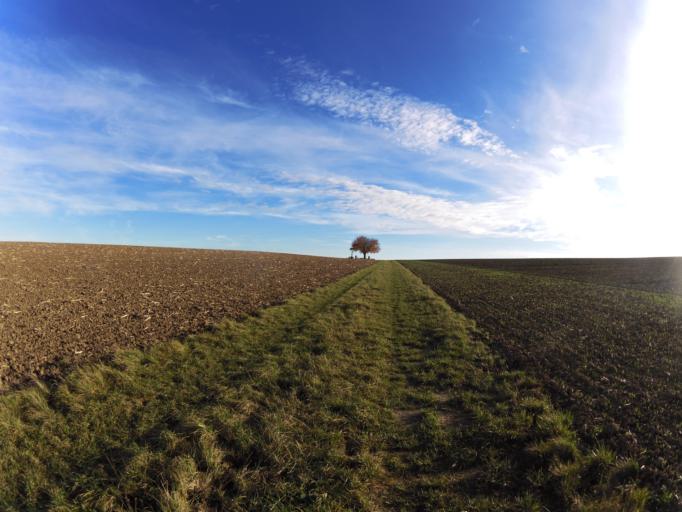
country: DE
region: Bavaria
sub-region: Regierungsbezirk Unterfranken
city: Giebelstadt
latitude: 49.6641
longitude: 9.9570
